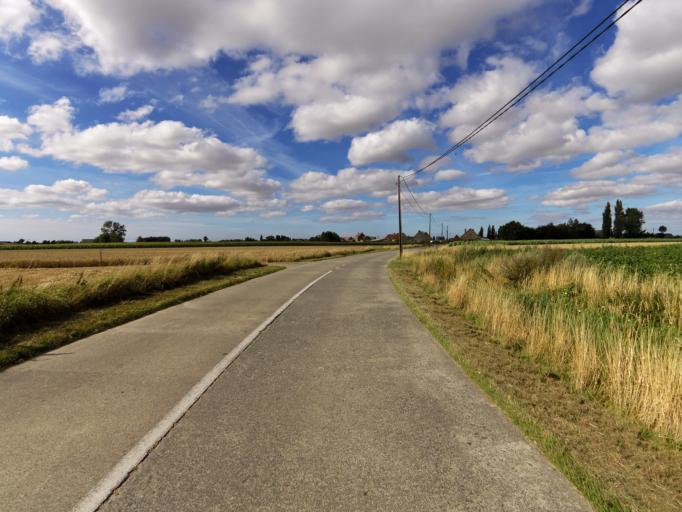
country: BE
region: Flanders
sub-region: Provincie West-Vlaanderen
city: Alveringem
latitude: 50.9783
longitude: 2.6605
